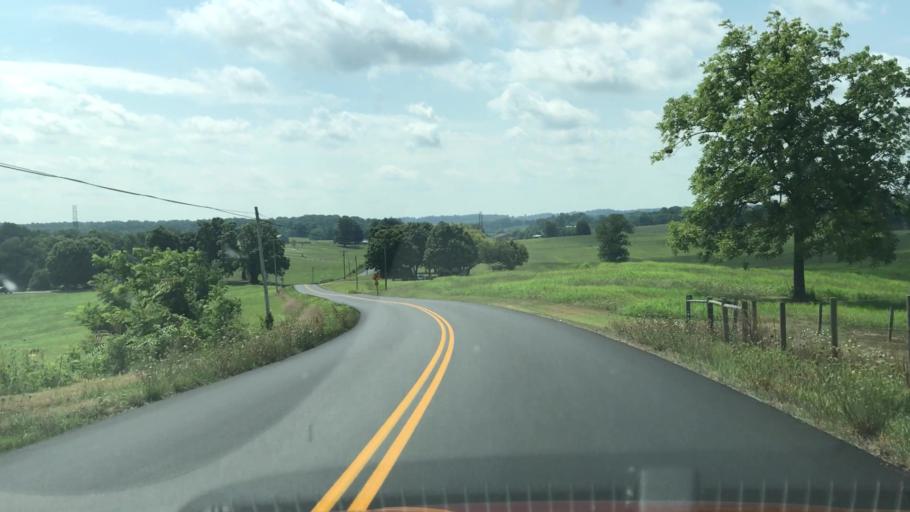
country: US
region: Kentucky
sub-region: Monroe County
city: Tompkinsville
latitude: 36.7992
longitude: -85.8198
